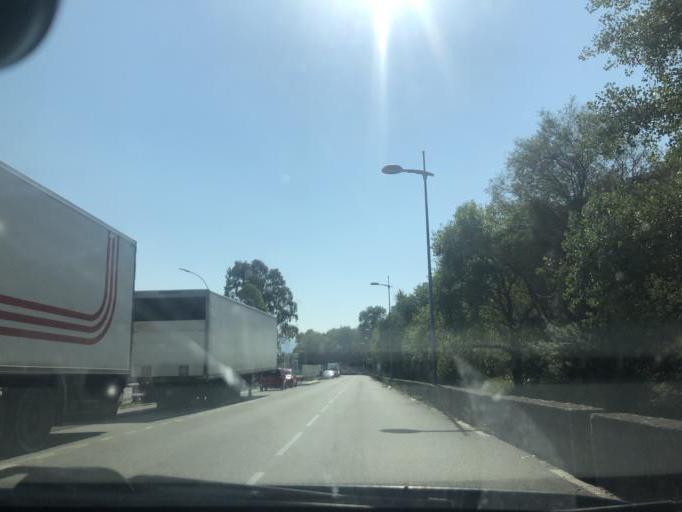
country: FR
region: Provence-Alpes-Cote d'Azur
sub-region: Departement des Alpes-Maritimes
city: Saint-Martin-du-Var
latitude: 43.8092
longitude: 7.1825
